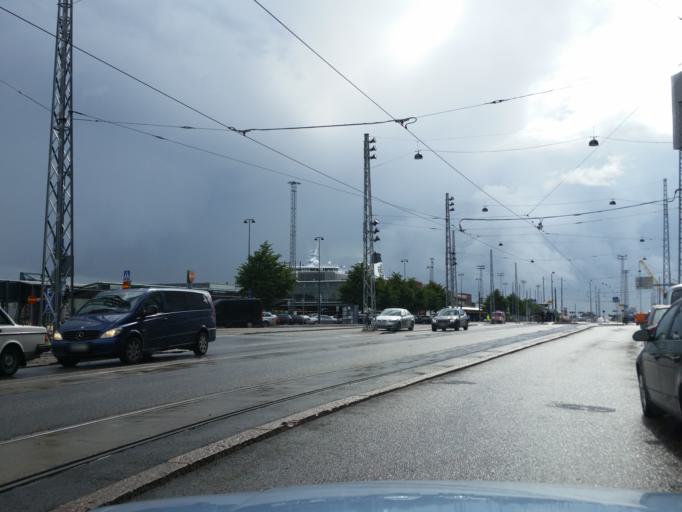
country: FI
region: Uusimaa
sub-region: Helsinki
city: Helsinki
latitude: 60.1567
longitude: 24.9220
